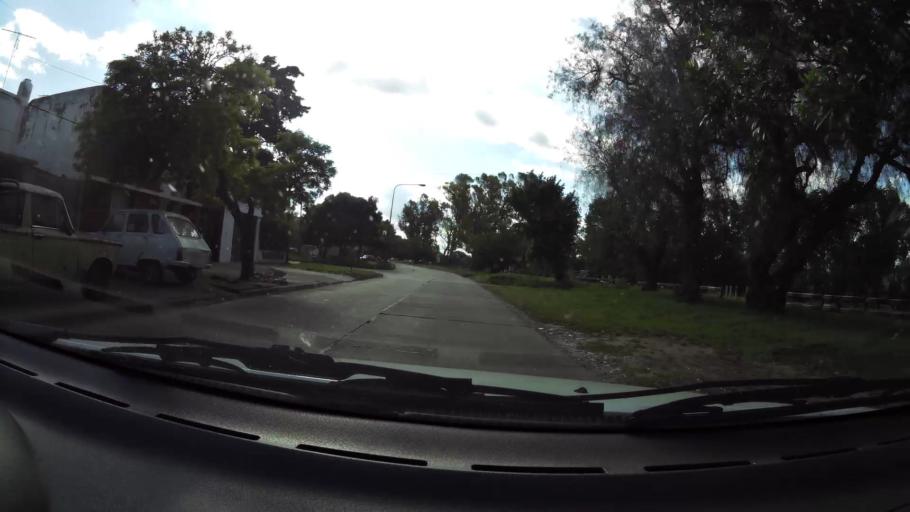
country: AR
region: Buenos Aires
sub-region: Partido de La Plata
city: La Plata
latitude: -34.8927
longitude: -57.9536
